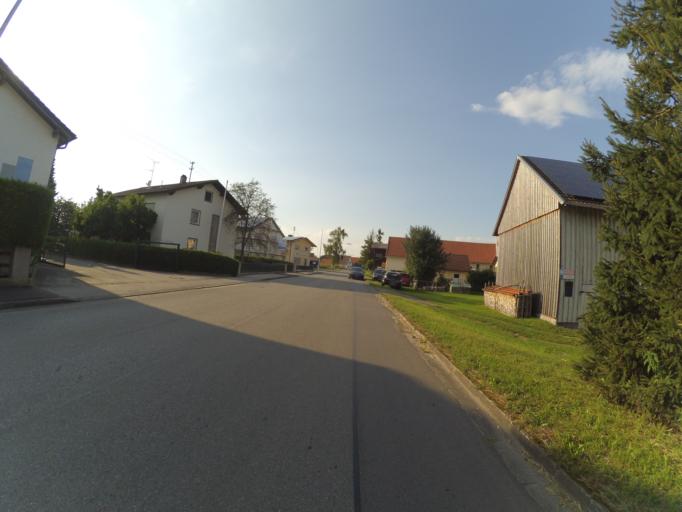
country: DE
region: Bavaria
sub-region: Swabia
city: Tussenhausen
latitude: 48.0646
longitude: 10.5818
